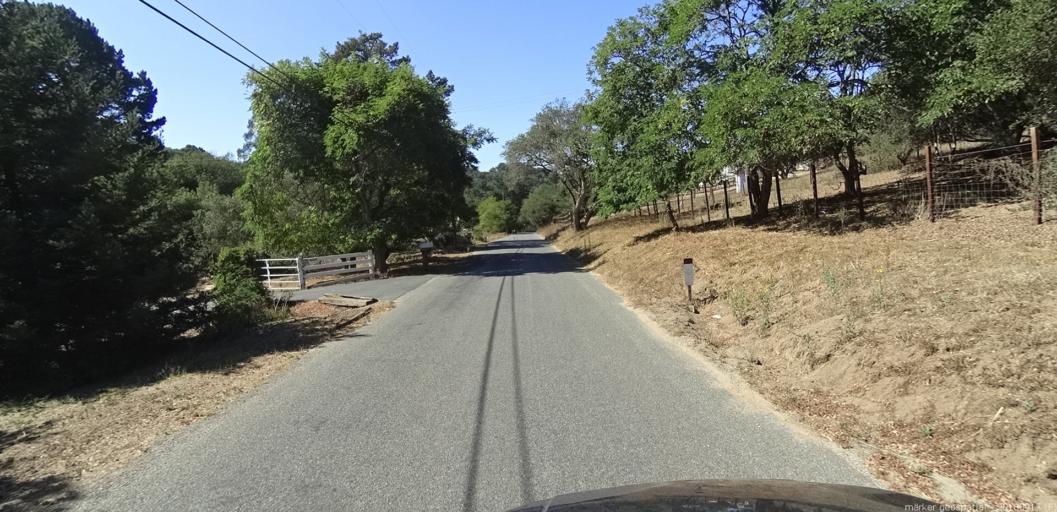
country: US
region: California
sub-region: Monterey County
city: Elkhorn
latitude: 36.8271
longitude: -121.6992
